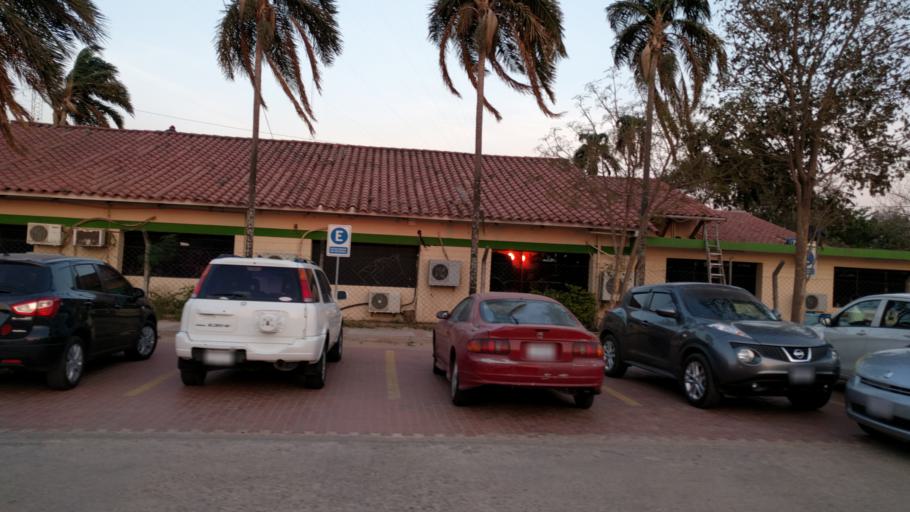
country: BO
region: Santa Cruz
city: Santa Cruz de la Sierra
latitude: -17.7587
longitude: -63.1480
